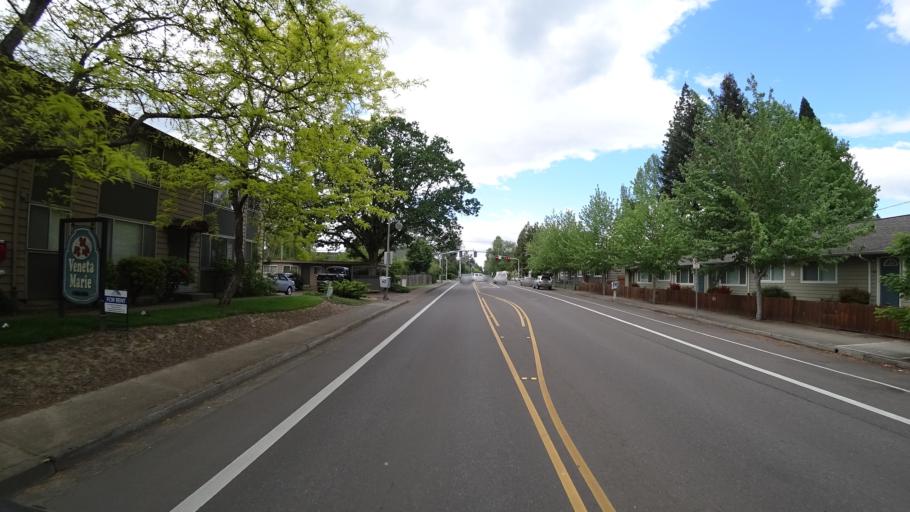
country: US
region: Oregon
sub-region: Washington County
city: Beaverton
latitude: 45.4828
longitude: -122.7994
